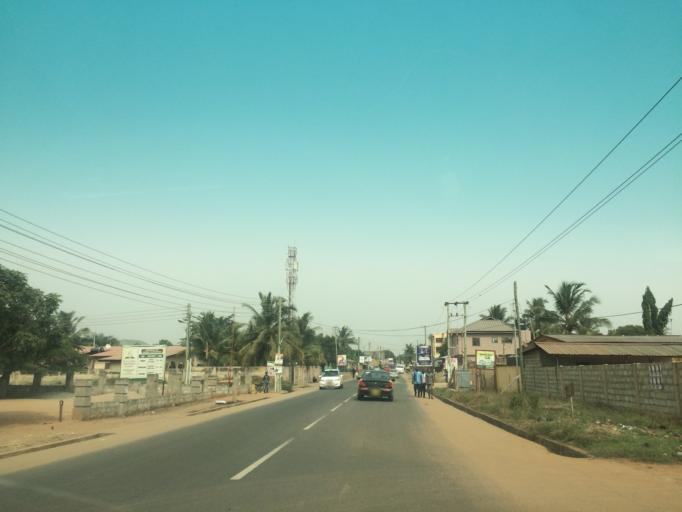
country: GH
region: Greater Accra
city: Nungua
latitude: 5.6095
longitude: -0.0870
